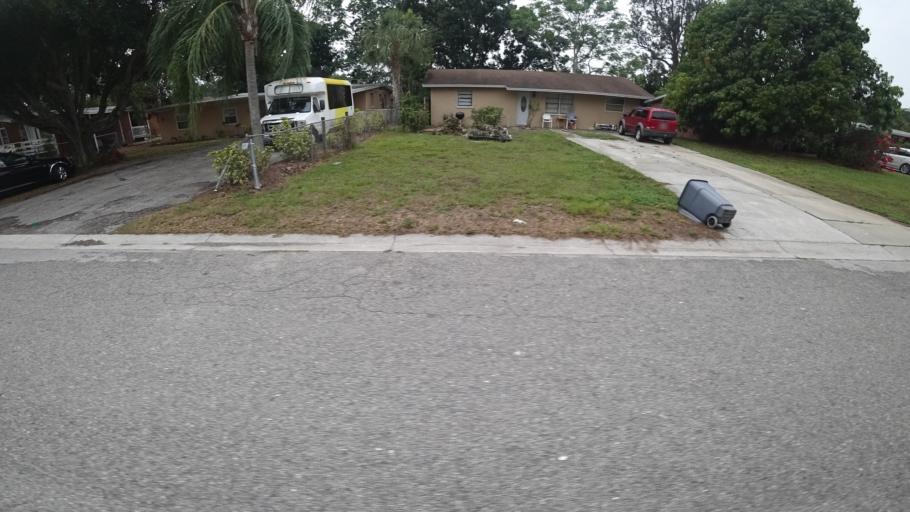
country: US
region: Florida
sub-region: Manatee County
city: Samoset
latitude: 27.4420
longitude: -82.5078
